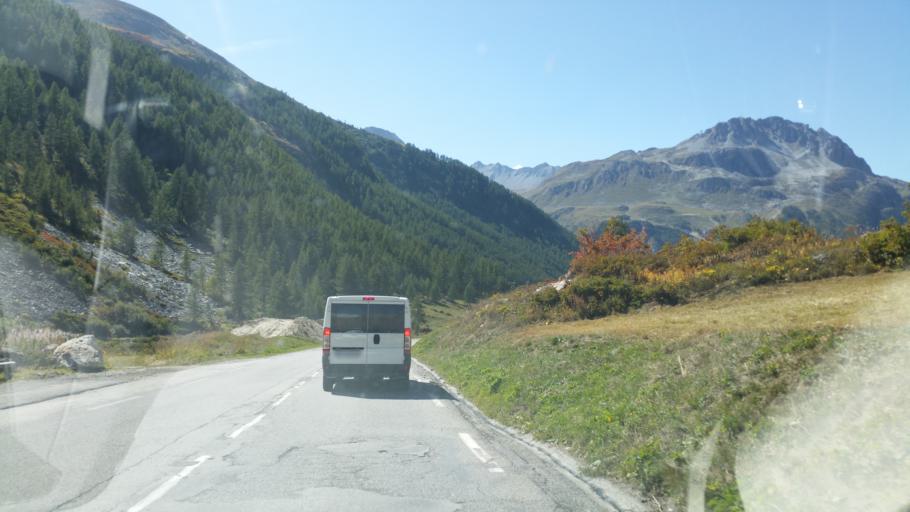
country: FR
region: Rhone-Alpes
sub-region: Departement de la Savoie
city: Val-d'Isere
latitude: 45.4488
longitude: 7.0078
